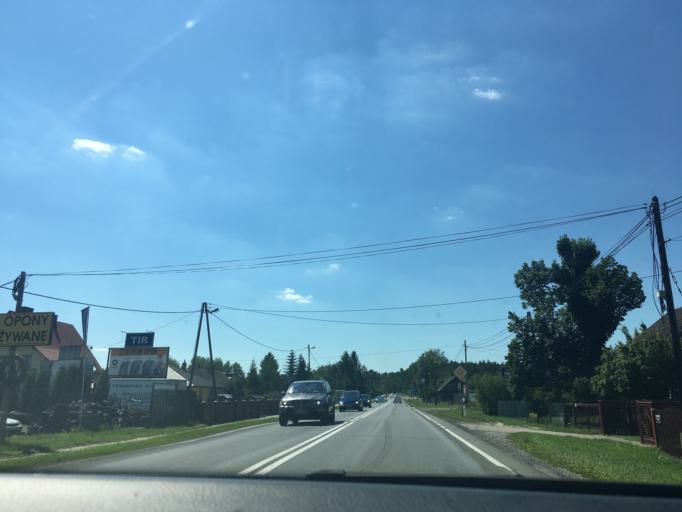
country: PL
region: Subcarpathian Voivodeship
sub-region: Powiat nizanski
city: Nisko
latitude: 50.5017
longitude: 22.1395
